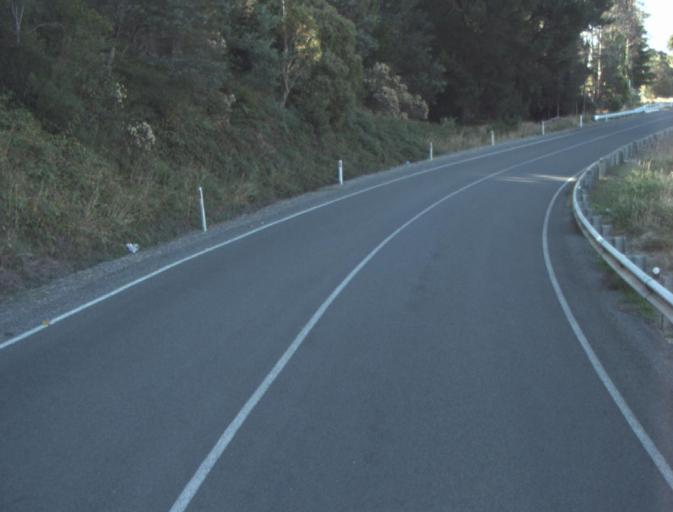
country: AU
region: Tasmania
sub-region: Launceston
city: Mayfield
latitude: -41.2302
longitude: 147.2095
